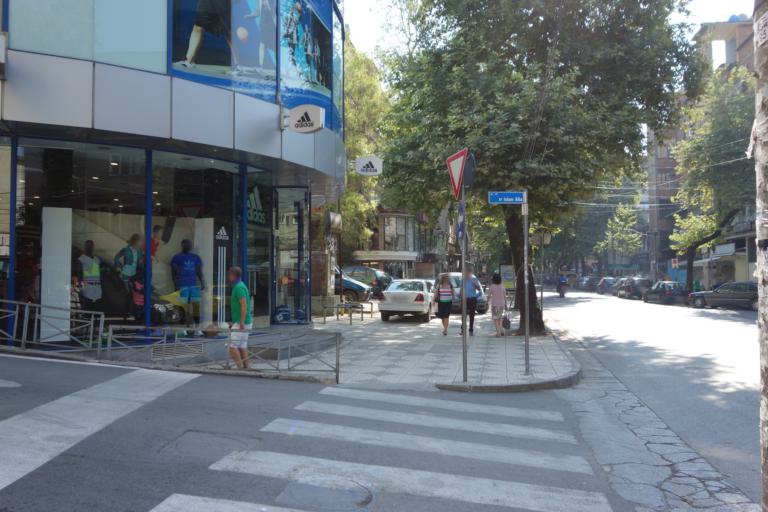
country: AL
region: Tirane
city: Tirana
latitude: 41.3249
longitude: 19.8118
